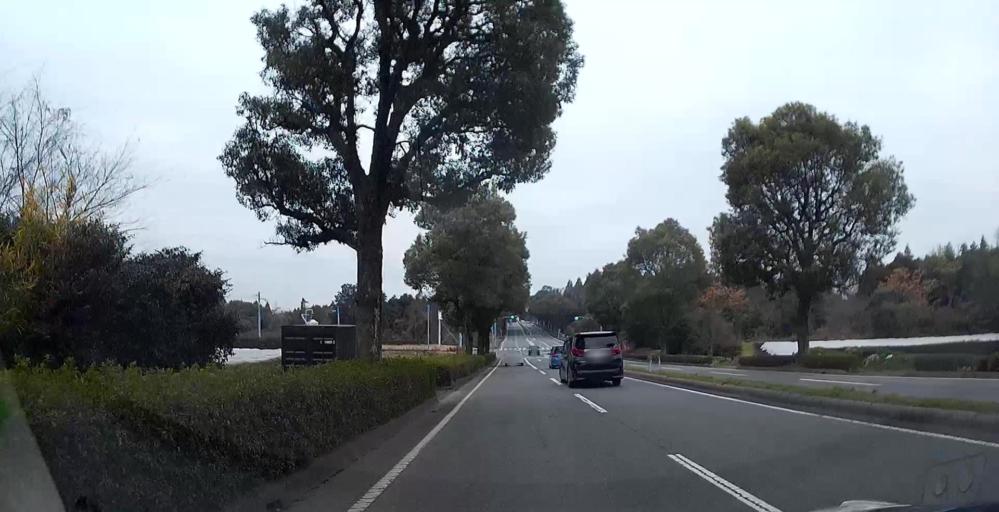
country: JP
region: Kumamoto
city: Ozu
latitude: 32.8067
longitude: 130.8105
